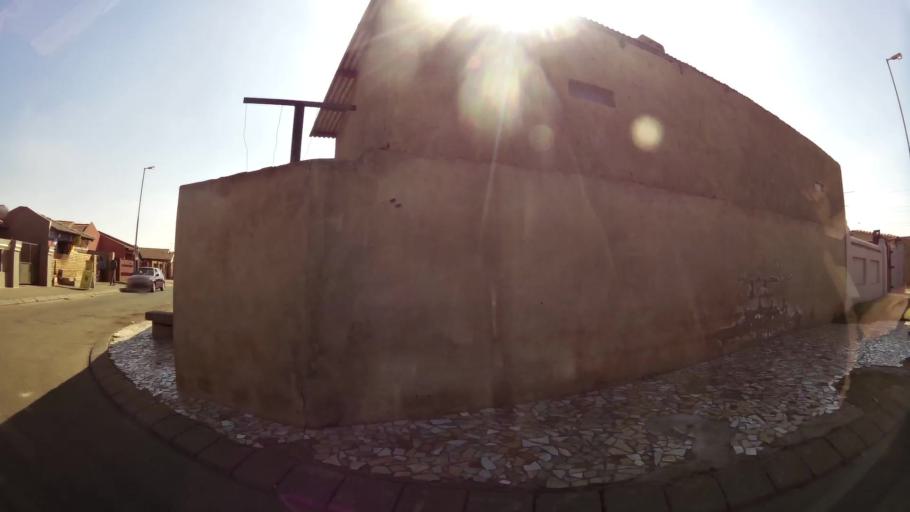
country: ZA
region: Gauteng
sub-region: City of Johannesburg Metropolitan Municipality
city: Soweto
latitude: -26.2905
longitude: 27.8557
